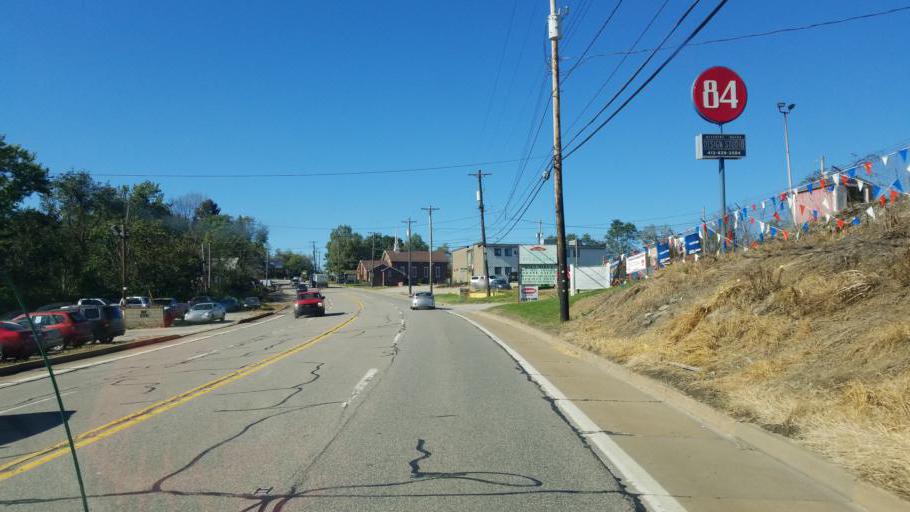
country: US
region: Pennsylvania
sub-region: Westmoreland County
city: Trafford
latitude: 40.3646
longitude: -79.7745
